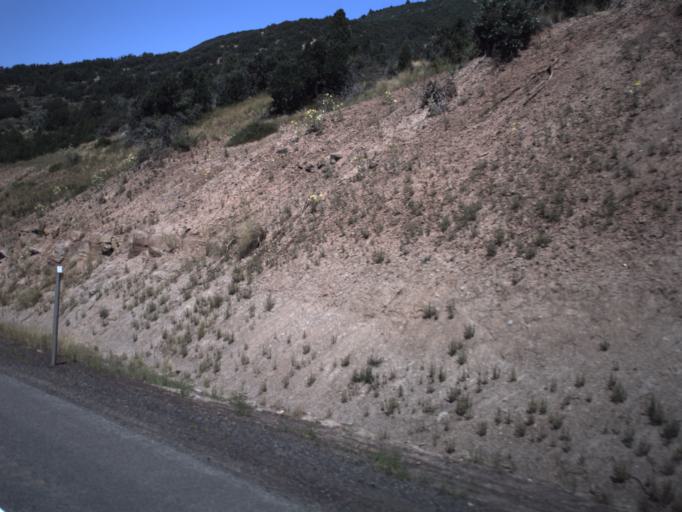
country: US
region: Utah
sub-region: Carbon County
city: Helper
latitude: 39.9341
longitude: -111.1019
